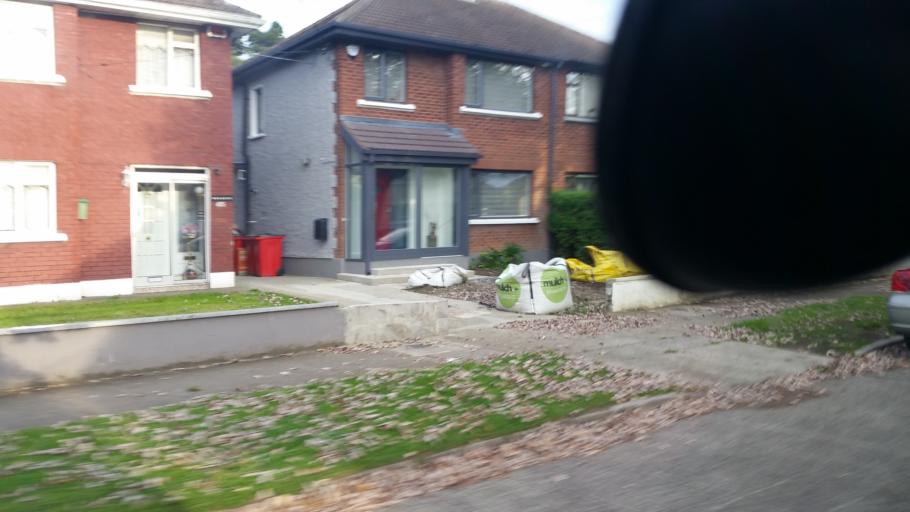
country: IE
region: Leinster
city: Beaumont
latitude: 53.3882
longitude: -6.2315
